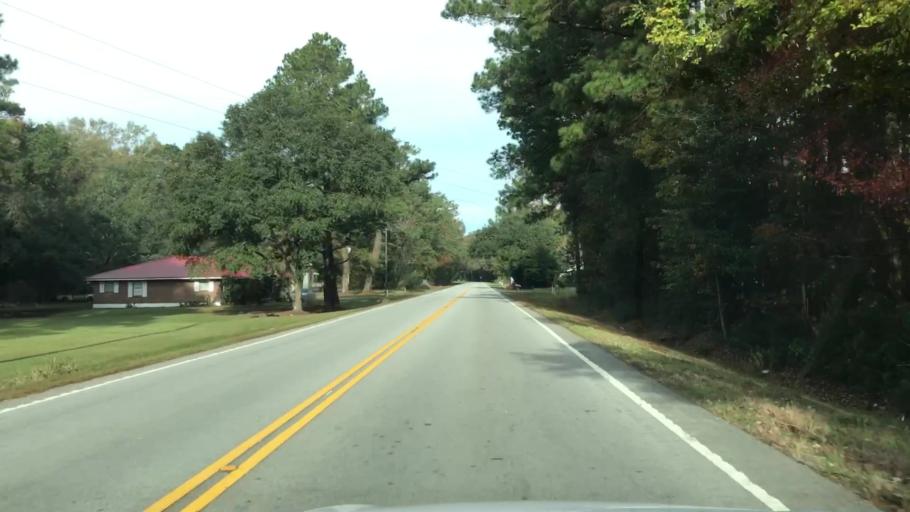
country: US
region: South Carolina
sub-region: Charleston County
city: Ravenel
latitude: 32.7770
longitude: -80.4631
